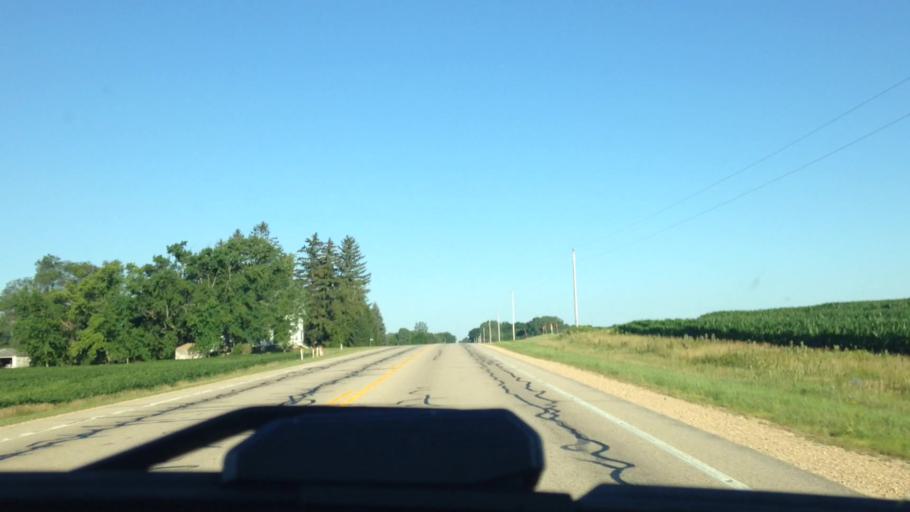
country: US
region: Wisconsin
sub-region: Columbia County
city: Fall River
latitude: 43.3406
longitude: -89.1314
